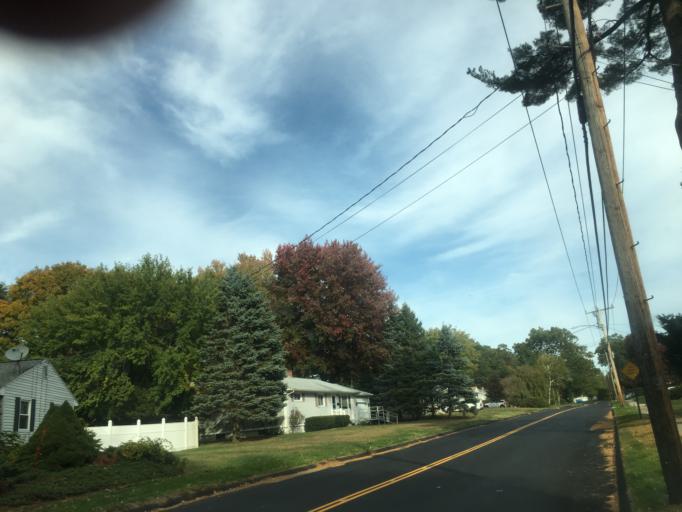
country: US
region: Connecticut
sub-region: Hartford County
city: Sherwood Manor
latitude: 42.0240
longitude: -72.5746
